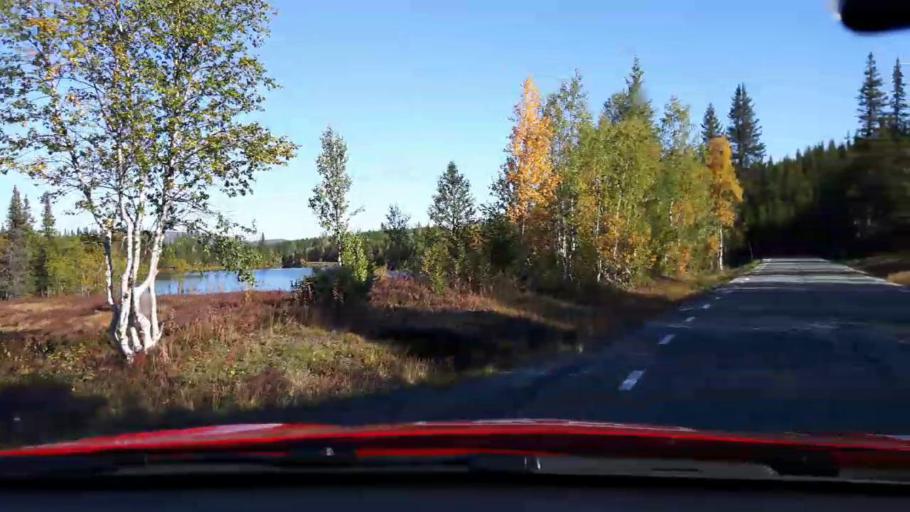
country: NO
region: Nord-Trondelag
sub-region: Lierne
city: Sandvika
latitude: 64.6101
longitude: 13.6995
